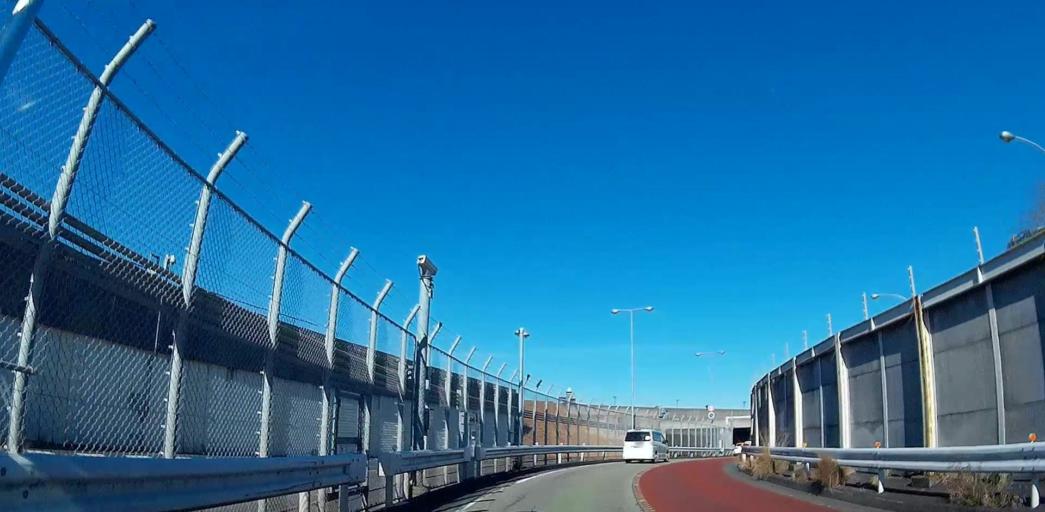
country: JP
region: Chiba
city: Narita
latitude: 35.7606
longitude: 140.3921
